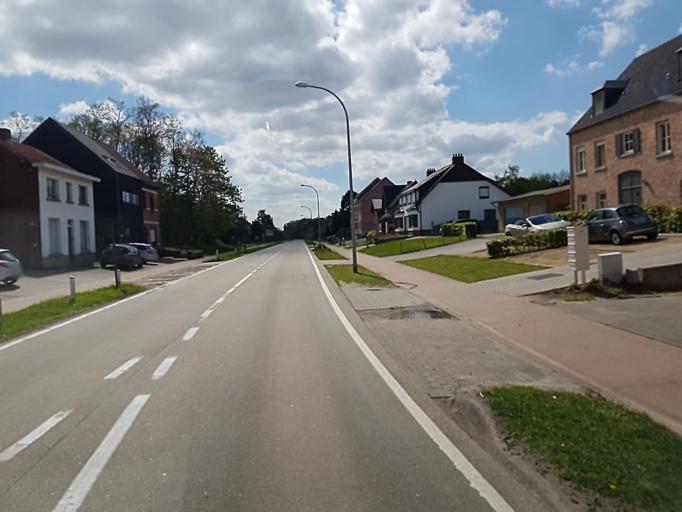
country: BE
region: Flanders
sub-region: Provincie Antwerpen
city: Westerlo
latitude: 51.0966
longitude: 4.9448
